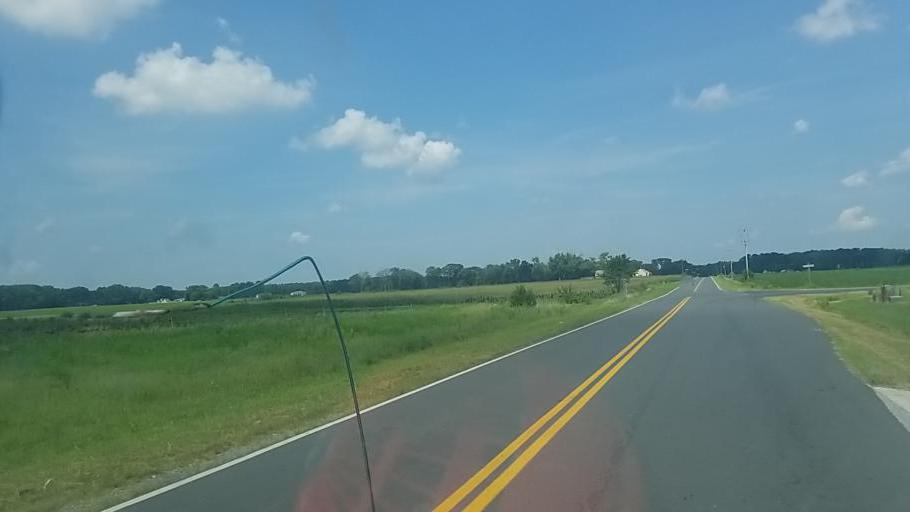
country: US
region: Maryland
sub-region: Wicomico County
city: Salisbury
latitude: 38.3470
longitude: -75.5205
